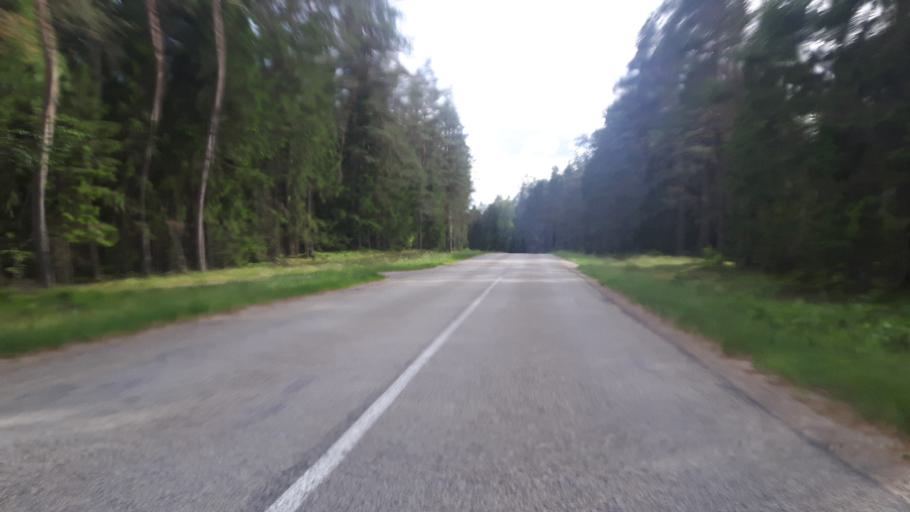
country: LV
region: Engure
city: Smarde
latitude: 57.0086
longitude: 23.3374
